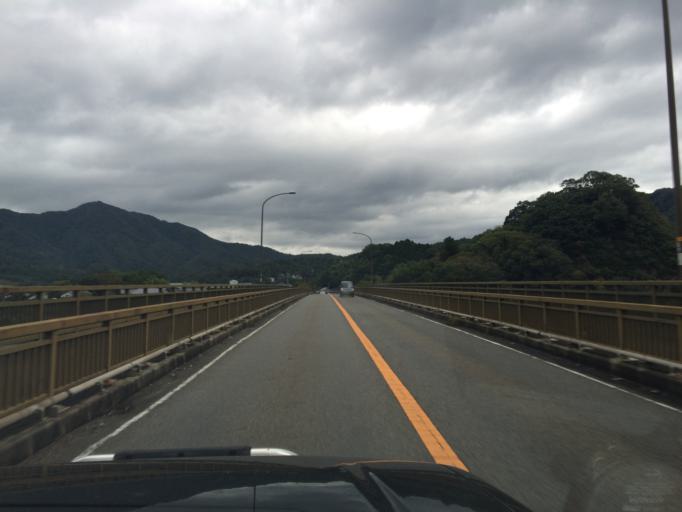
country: JP
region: Hyogo
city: Toyooka
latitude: 35.4266
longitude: 134.7923
